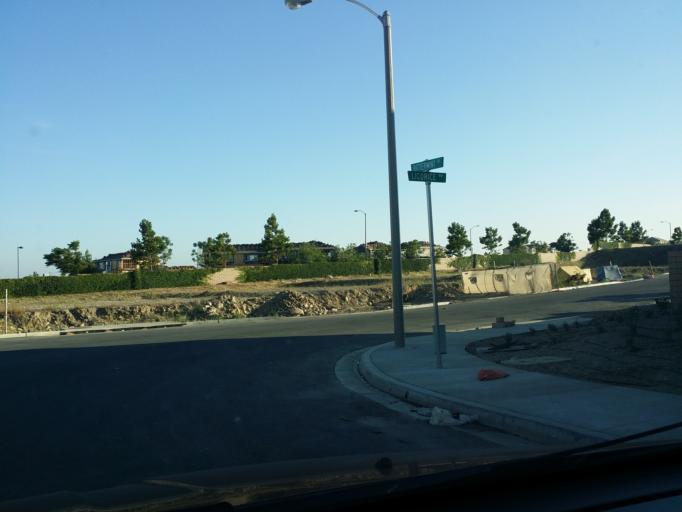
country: US
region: California
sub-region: San Bernardino County
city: Muscoy
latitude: 34.1901
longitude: -117.4183
